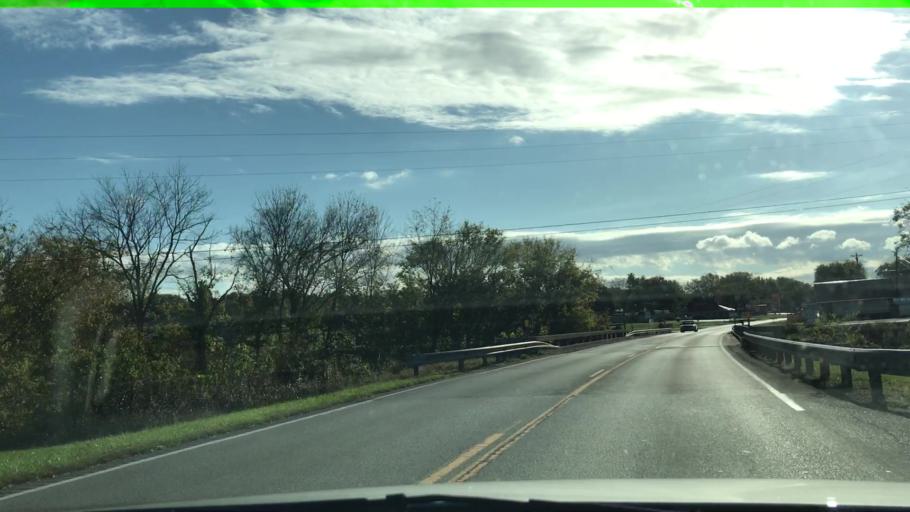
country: US
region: Kentucky
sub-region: Metcalfe County
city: Edmonton
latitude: 36.9877
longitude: -85.6350
